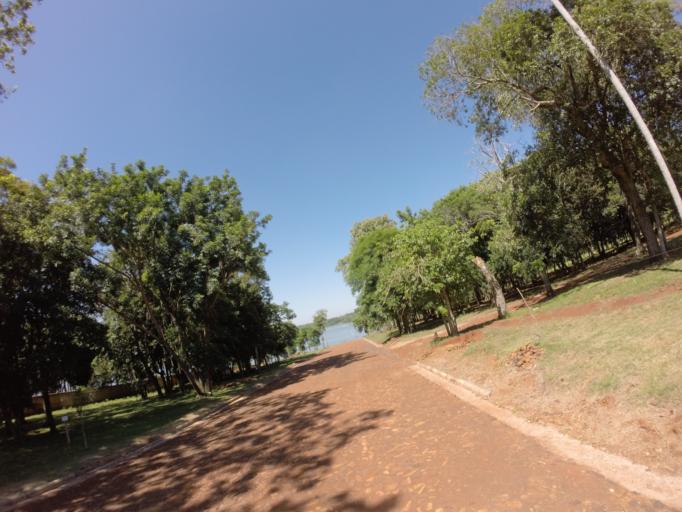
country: PY
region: Alto Parana
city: Ciudad del Este
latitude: -25.4399
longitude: -54.6495
